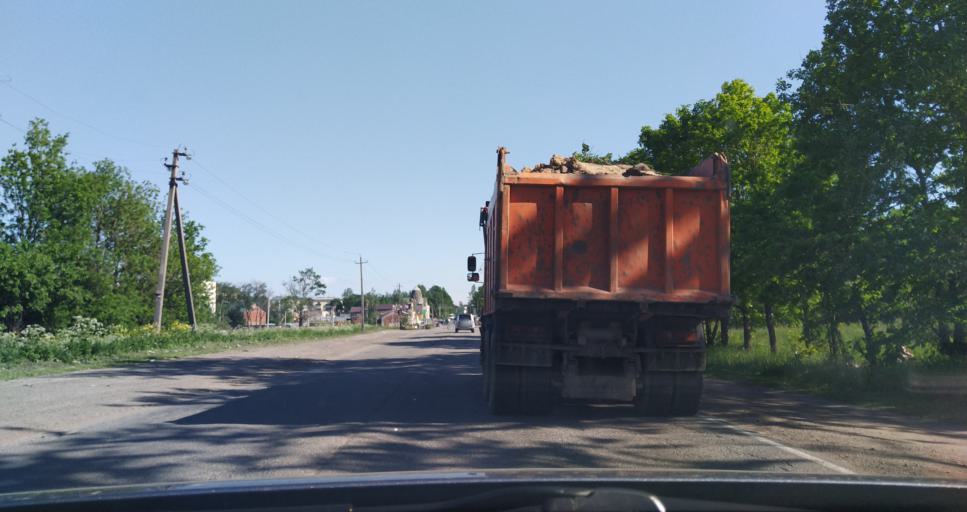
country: RU
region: St.-Petersburg
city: Krasnoye Selo
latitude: 59.7009
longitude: 30.0988
